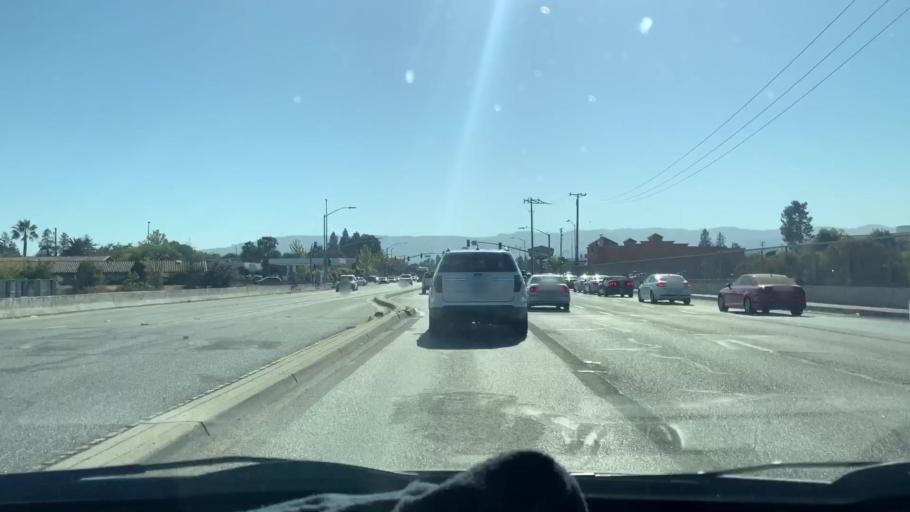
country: US
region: California
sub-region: Santa Clara County
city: Campbell
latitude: 37.3177
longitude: -121.9746
